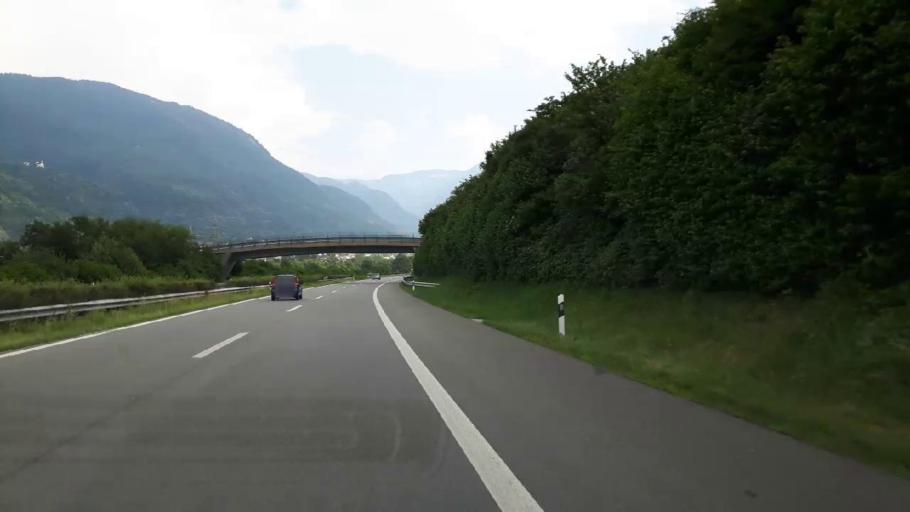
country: CH
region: Ticino
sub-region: Riviera District
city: Claro
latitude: 46.2682
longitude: 9.0048
